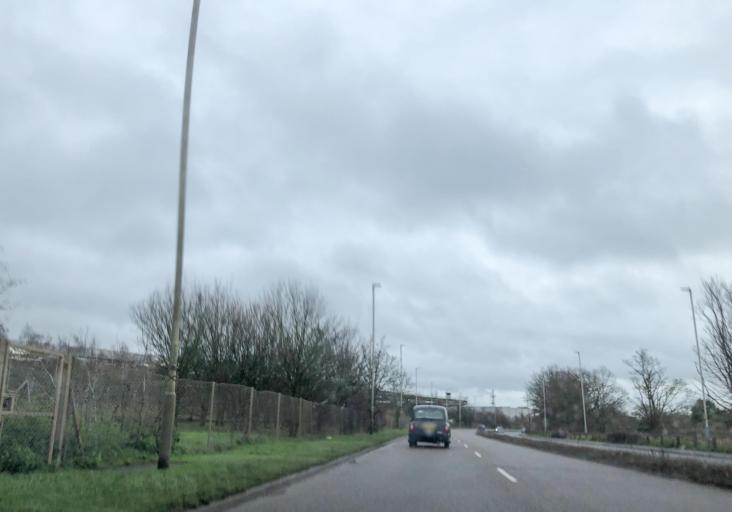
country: GB
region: England
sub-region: Buckinghamshire
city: Iver
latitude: 51.4727
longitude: -0.4943
